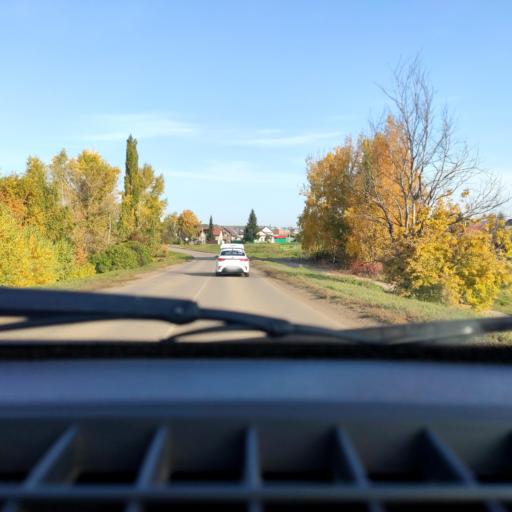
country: RU
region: Bashkortostan
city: Avdon
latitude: 54.6527
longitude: 55.7776
